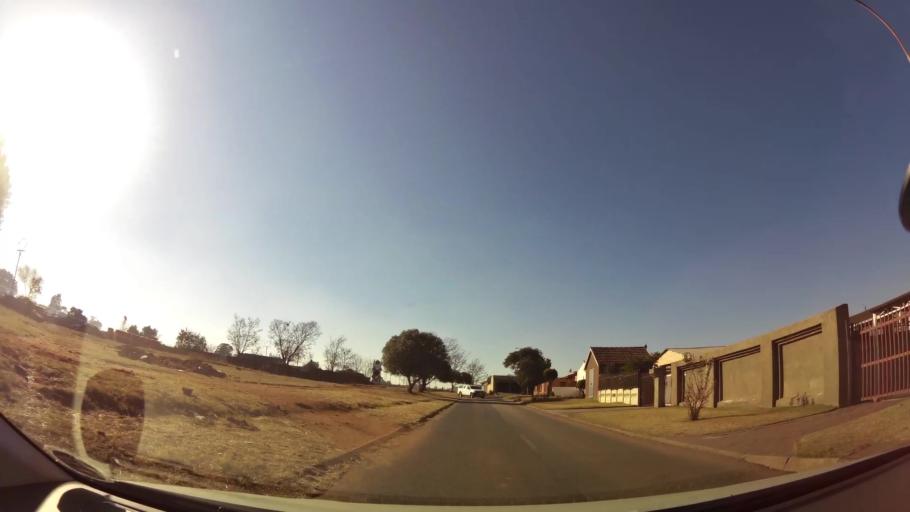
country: ZA
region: Gauteng
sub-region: City of Johannesburg Metropolitan Municipality
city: Johannesburg
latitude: -26.2034
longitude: 27.9598
